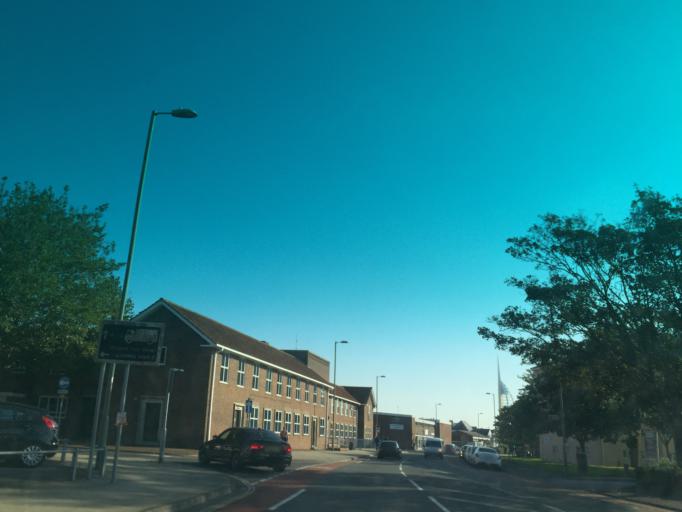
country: GB
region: England
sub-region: Hampshire
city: Gosport
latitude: 50.7942
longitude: -1.1242
